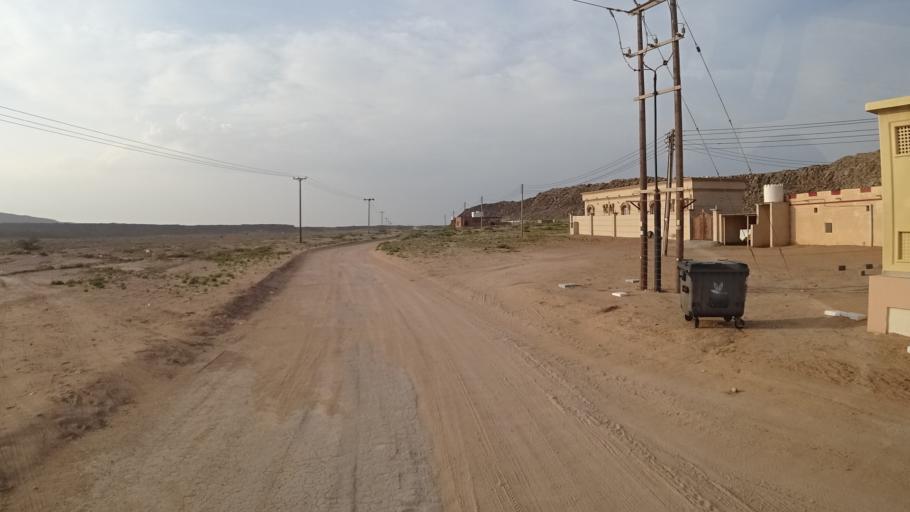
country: OM
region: Ash Sharqiyah
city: Sur
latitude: 22.4384
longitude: 59.8282
